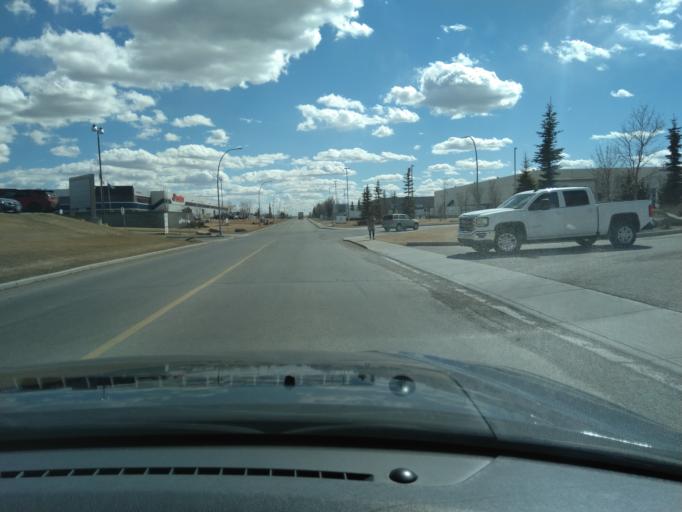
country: CA
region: Alberta
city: Calgary
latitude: 51.1219
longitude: -114.0372
